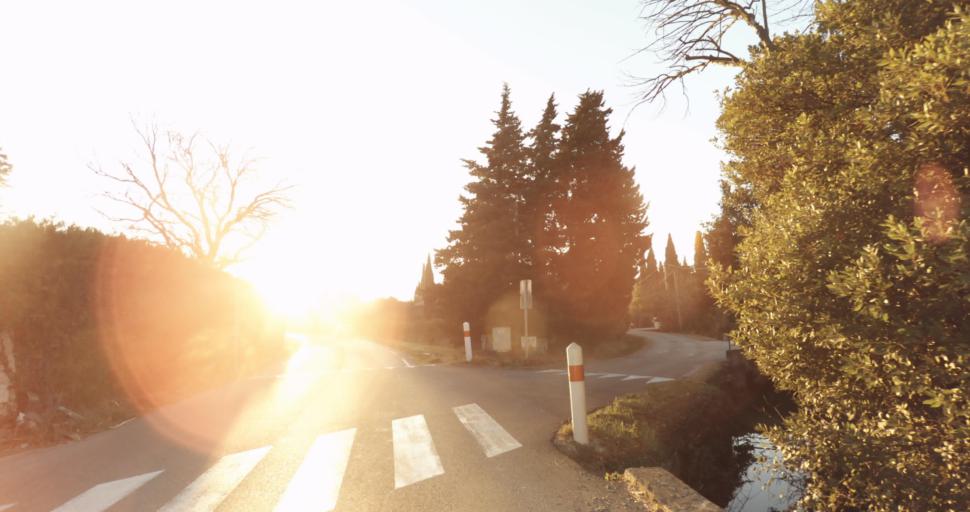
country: FR
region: Provence-Alpes-Cote d'Azur
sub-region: Departement des Bouches-du-Rhone
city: Barbentane
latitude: 43.8987
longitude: 4.7658
